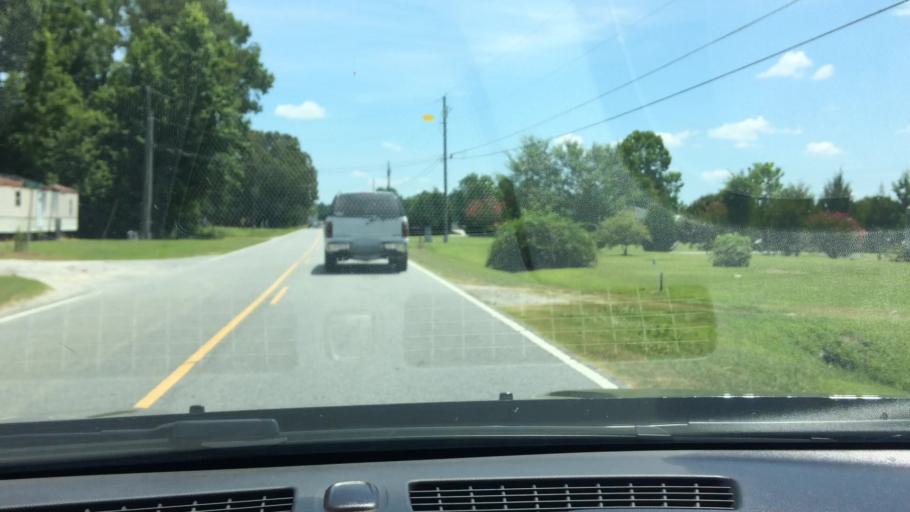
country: US
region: North Carolina
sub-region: Pitt County
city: Windsor
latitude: 35.5466
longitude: -77.2723
